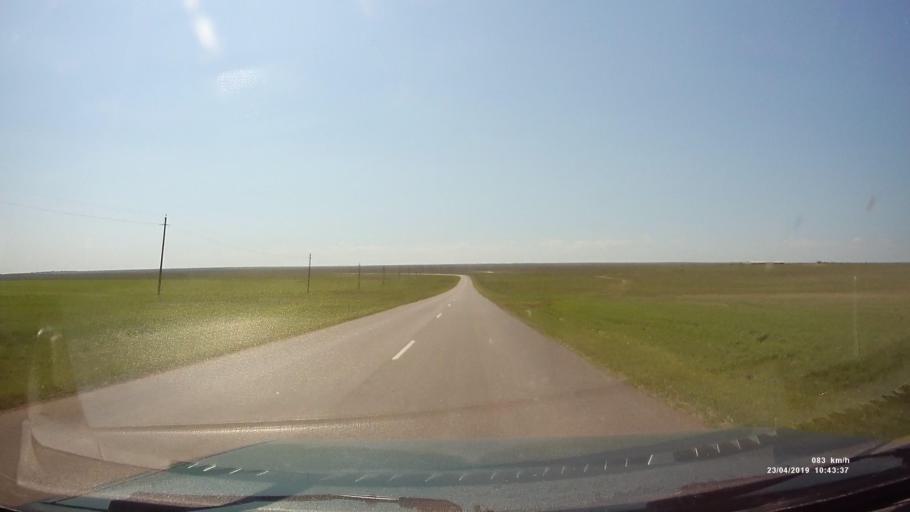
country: RU
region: Kalmykiya
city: Yashalta
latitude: 46.4681
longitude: 42.6501
